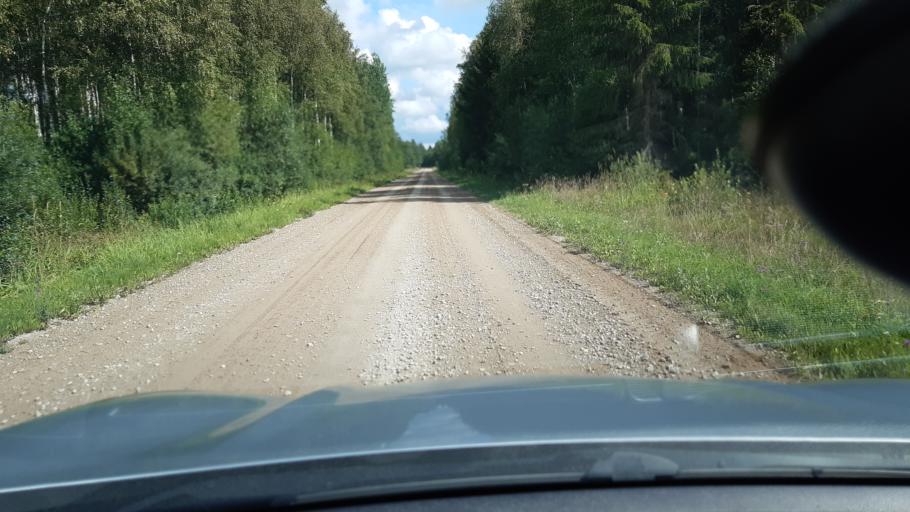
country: EE
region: Jaervamaa
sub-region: Tueri vald
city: Tueri
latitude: 58.9133
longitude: 25.1678
